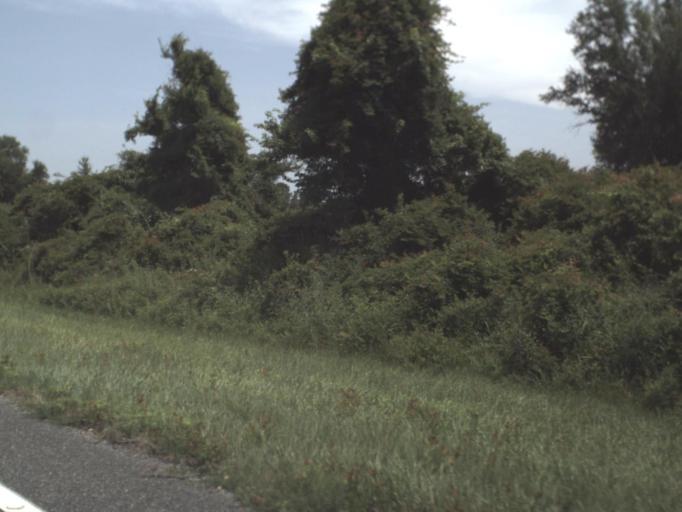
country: US
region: Florida
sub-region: Taylor County
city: Steinhatchee
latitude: 29.8266
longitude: -83.3575
